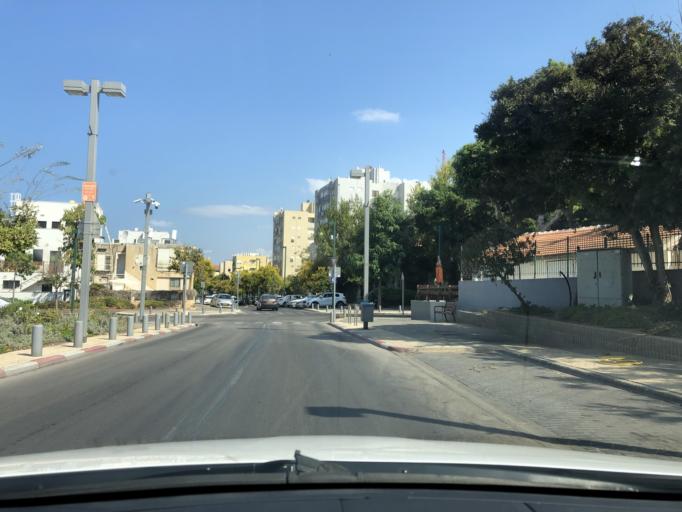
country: IL
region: Tel Aviv
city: Yafo
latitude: 32.0412
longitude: 34.7559
